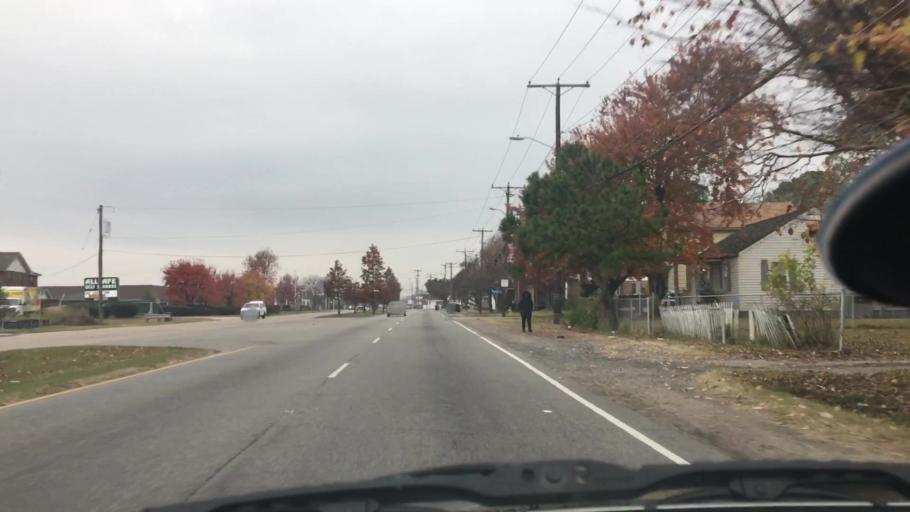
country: US
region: Virginia
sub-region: City of Norfolk
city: Norfolk
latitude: 36.8657
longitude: -76.2385
